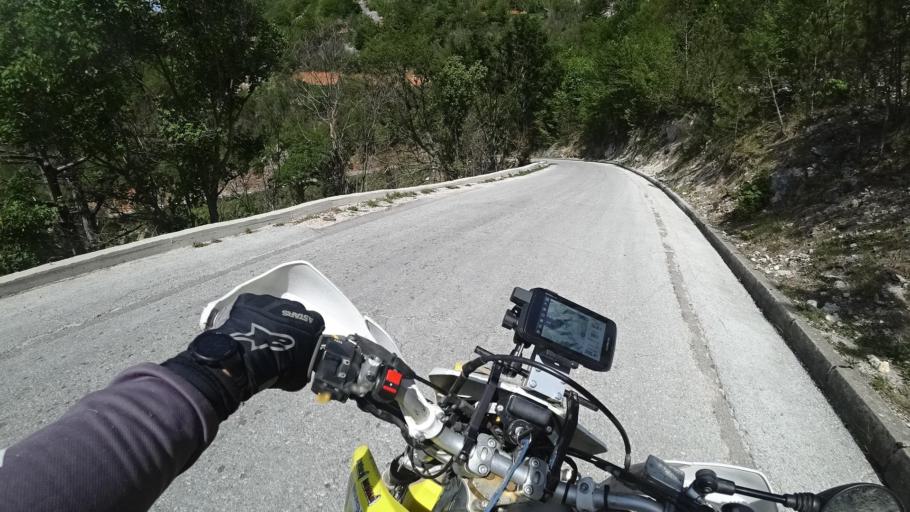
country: BA
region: Federation of Bosnia and Herzegovina
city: Potoci
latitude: 43.4577
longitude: 17.9566
